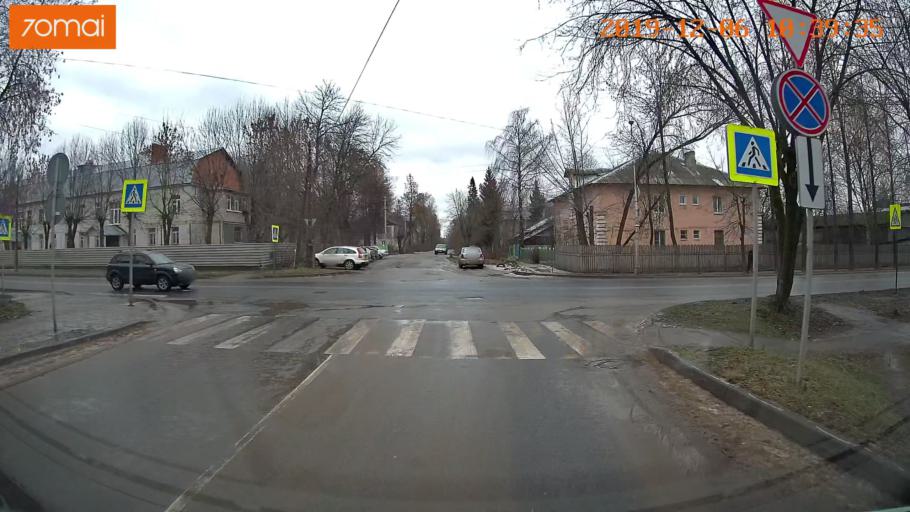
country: RU
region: Ivanovo
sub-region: Gorod Ivanovo
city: Ivanovo
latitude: 57.0303
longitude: 40.9751
